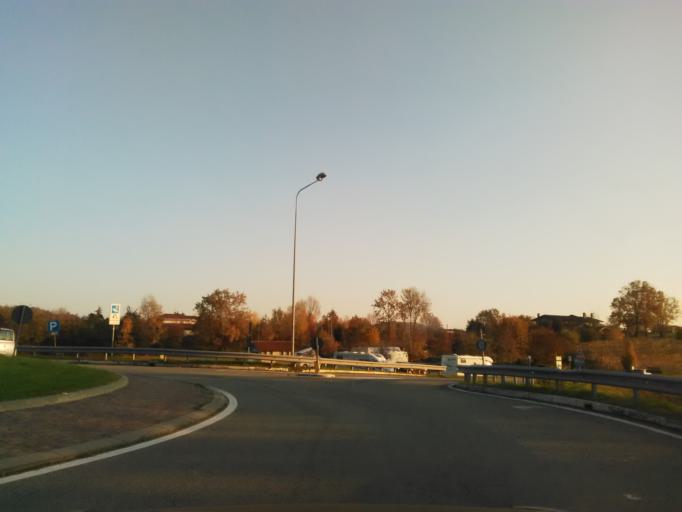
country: IT
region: Piedmont
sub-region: Provincia di Biella
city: Viverone
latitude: 45.4211
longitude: 8.0573
